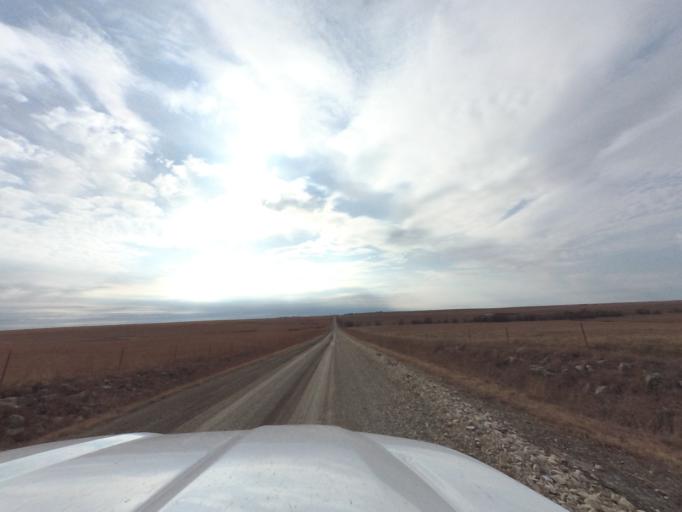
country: US
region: Kansas
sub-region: Chase County
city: Cottonwood Falls
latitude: 38.2305
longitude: -96.7307
